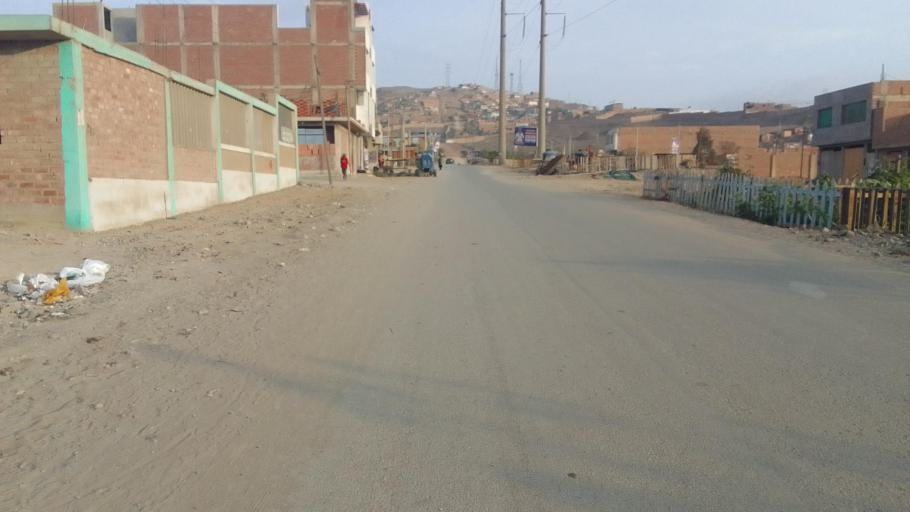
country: PE
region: Lima
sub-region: Lima
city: Santa Rosa
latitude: -11.8166
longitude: -77.1234
